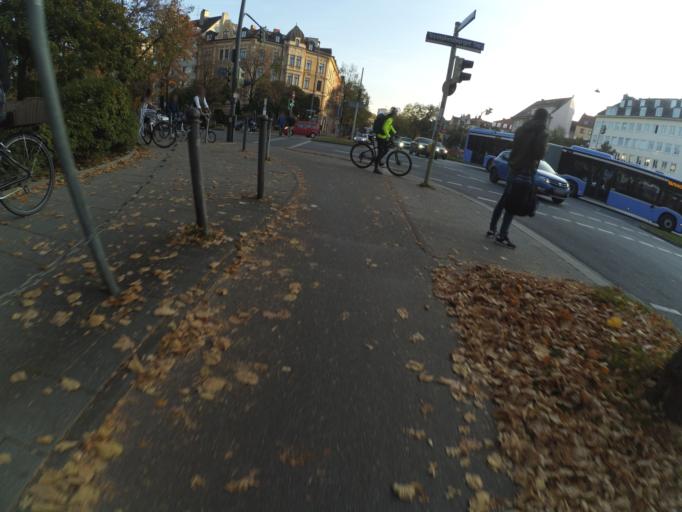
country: DE
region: Bavaria
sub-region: Upper Bavaria
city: Munich
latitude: 48.1519
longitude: 11.5373
